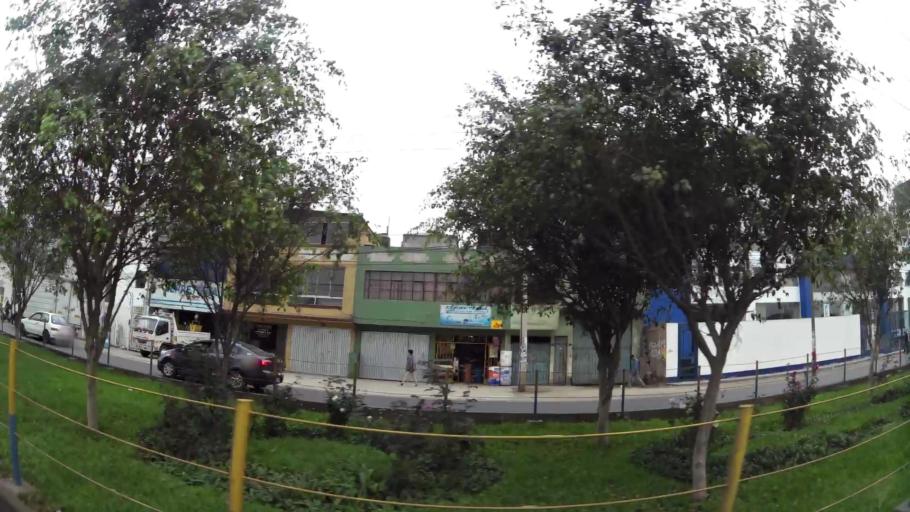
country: PE
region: Lima
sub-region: Lima
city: Independencia
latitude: -11.9836
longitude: -77.0102
